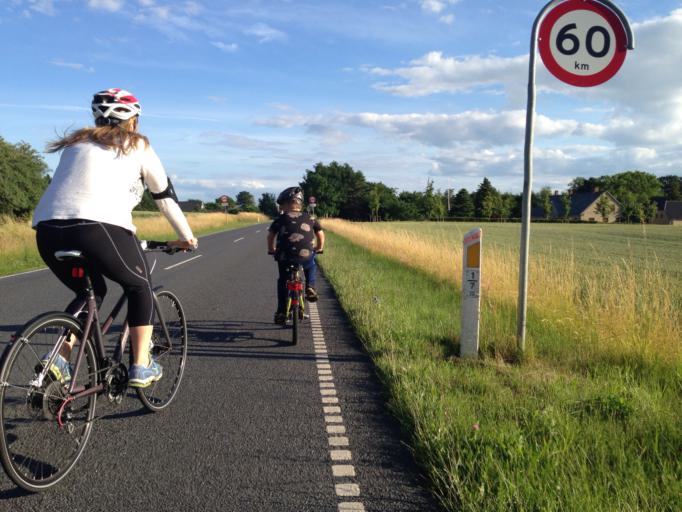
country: DK
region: South Denmark
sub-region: Middelfart Kommune
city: Norre Aby
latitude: 55.4841
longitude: 9.9021
